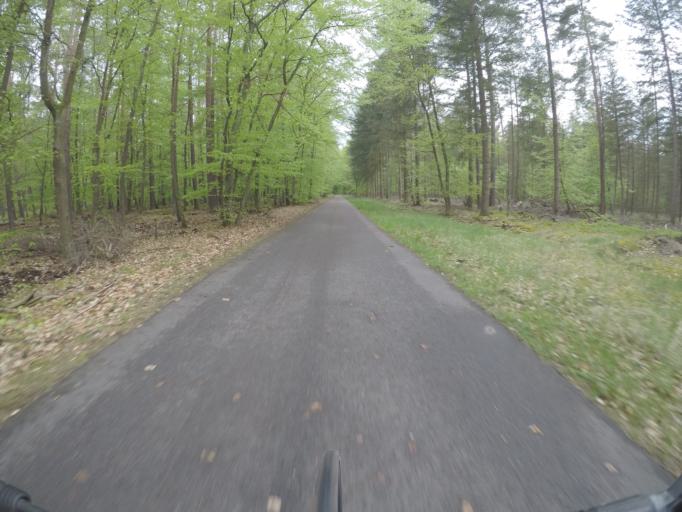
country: DE
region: Brandenburg
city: Biesenthal
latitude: 52.8053
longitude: 13.6295
